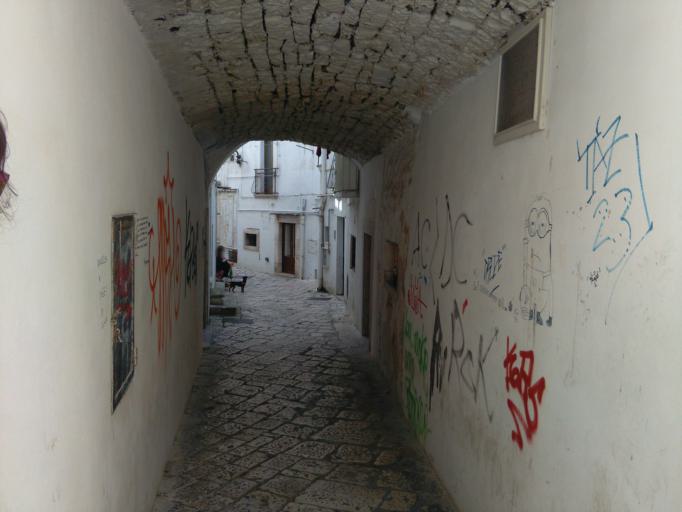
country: IT
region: Apulia
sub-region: Provincia di Bari
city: Putignano
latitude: 40.8504
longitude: 17.1230
